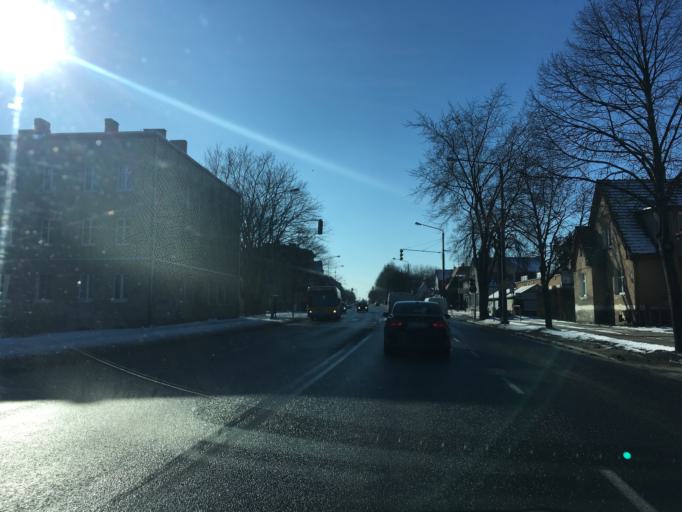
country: PL
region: Pomeranian Voivodeship
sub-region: Powiat slupski
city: Kobylnica
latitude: 54.4616
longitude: 17.0049
